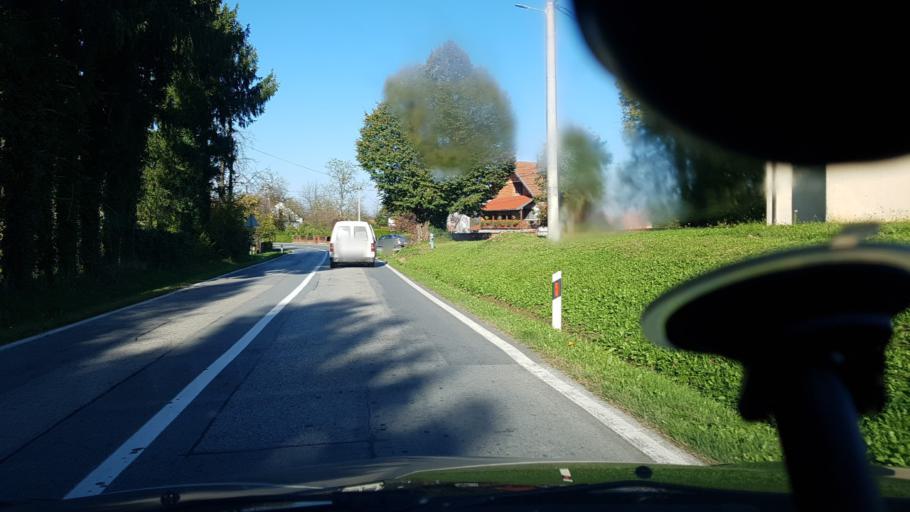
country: HR
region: Bjelovarsko-Bilogorska
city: Gudovac
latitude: 45.8005
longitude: 16.7177
